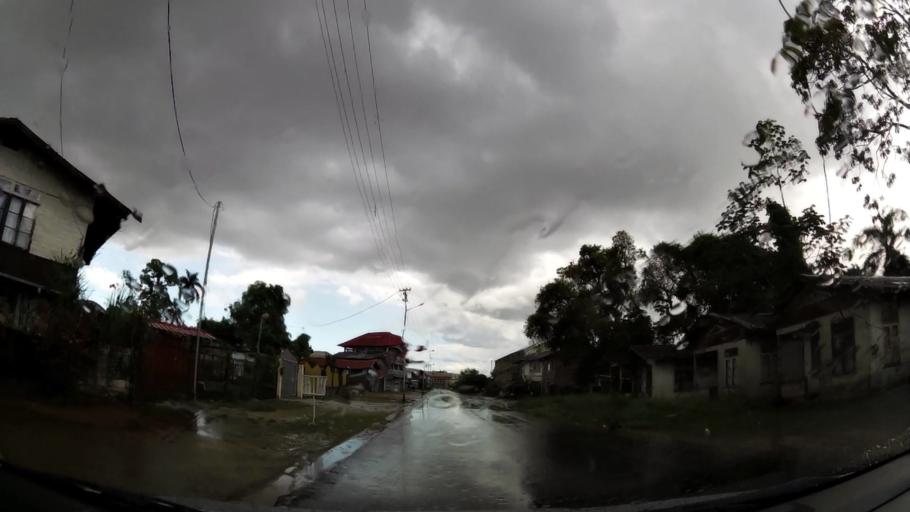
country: SR
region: Paramaribo
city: Paramaribo
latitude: 5.8242
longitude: -55.1710
